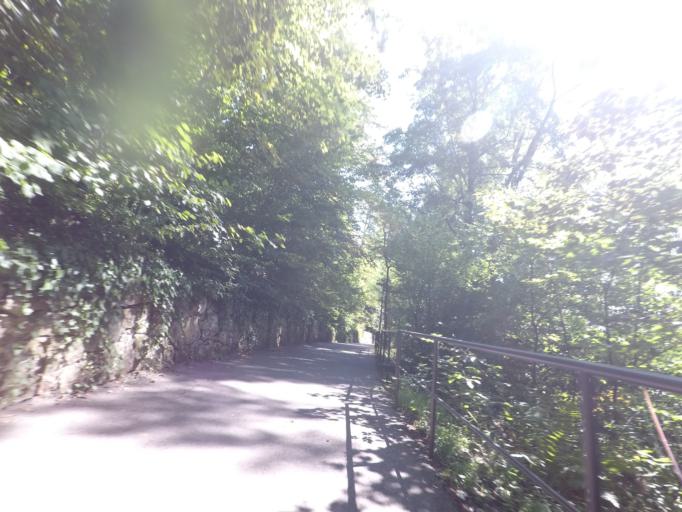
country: LU
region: Luxembourg
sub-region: Canton de Luxembourg
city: Luxembourg
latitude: 49.6236
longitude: 6.1322
